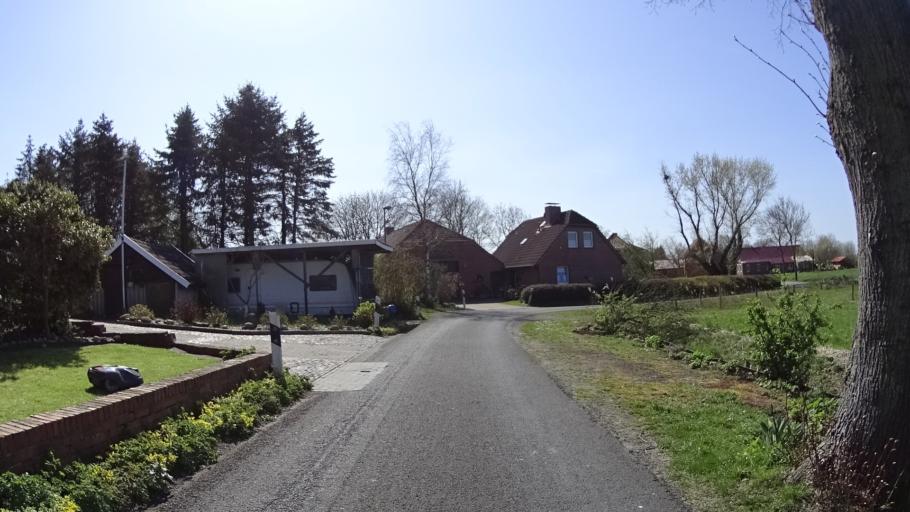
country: DE
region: Lower Saxony
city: Leer
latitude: 53.2036
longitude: 7.4042
